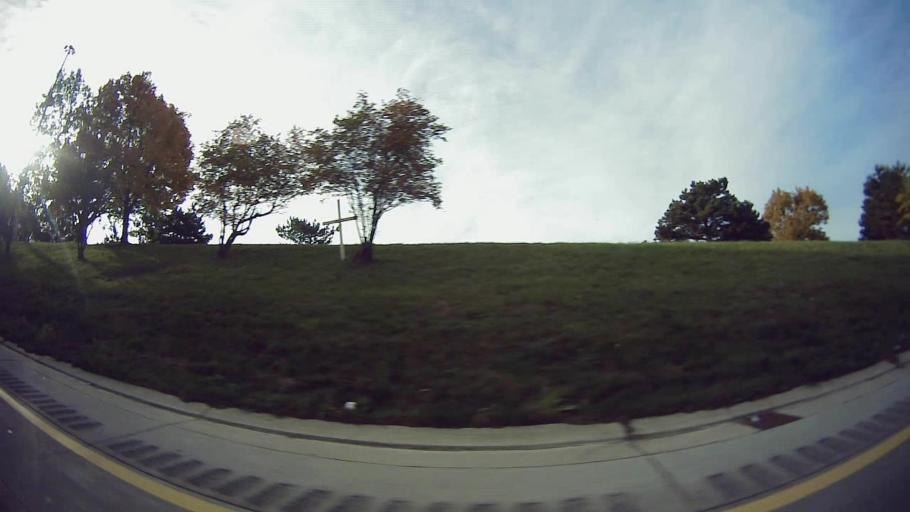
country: US
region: Michigan
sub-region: Wayne County
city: Detroit
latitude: 42.3333
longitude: -83.0861
